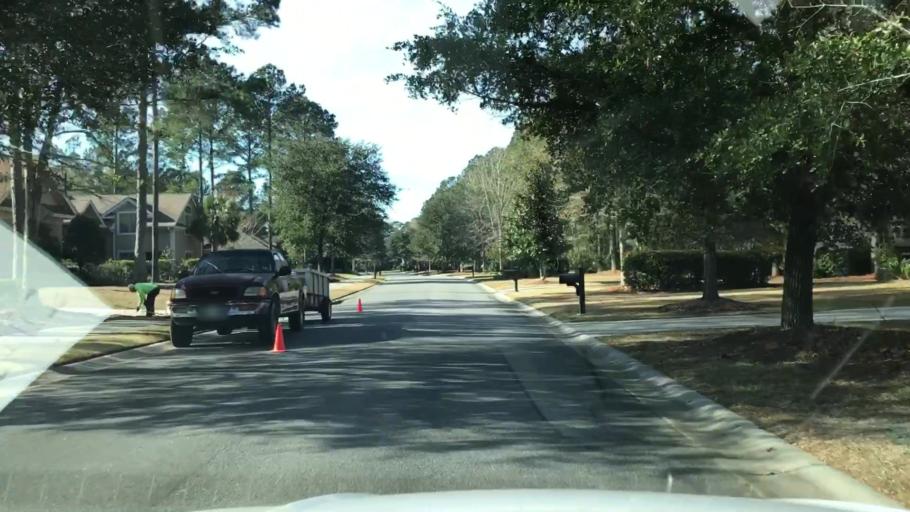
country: US
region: South Carolina
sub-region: Beaufort County
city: Bluffton
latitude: 32.2532
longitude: -80.9105
